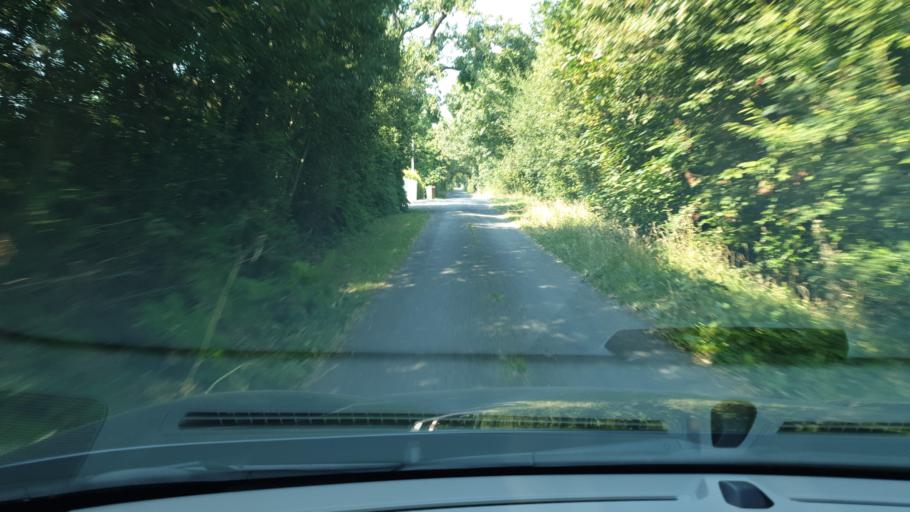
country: IE
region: Leinster
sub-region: An Mhi
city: Athboy
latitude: 53.6129
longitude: -6.9925
